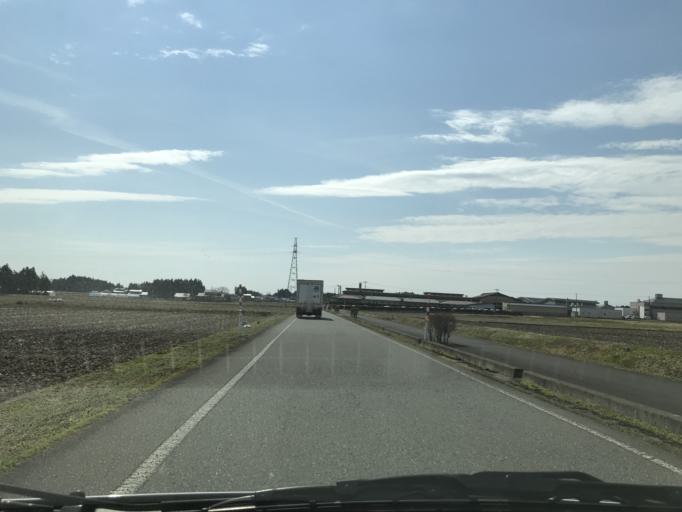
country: JP
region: Iwate
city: Mizusawa
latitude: 39.1319
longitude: 141.0700
